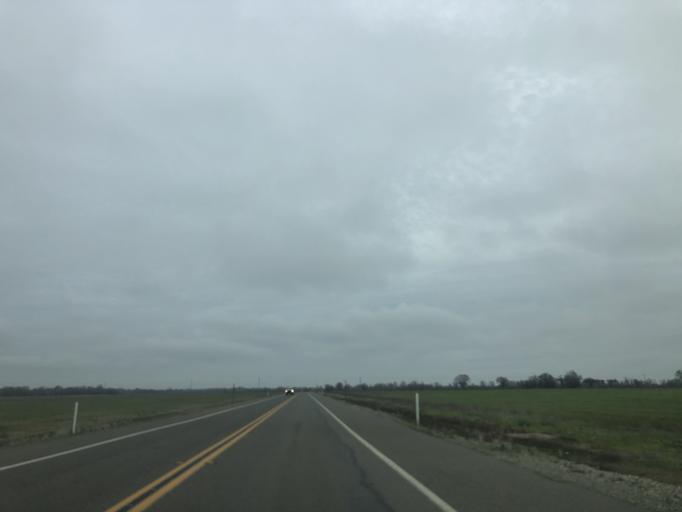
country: US
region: California
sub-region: Sacramento County
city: Elverta
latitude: 38.7097
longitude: -121.5901
